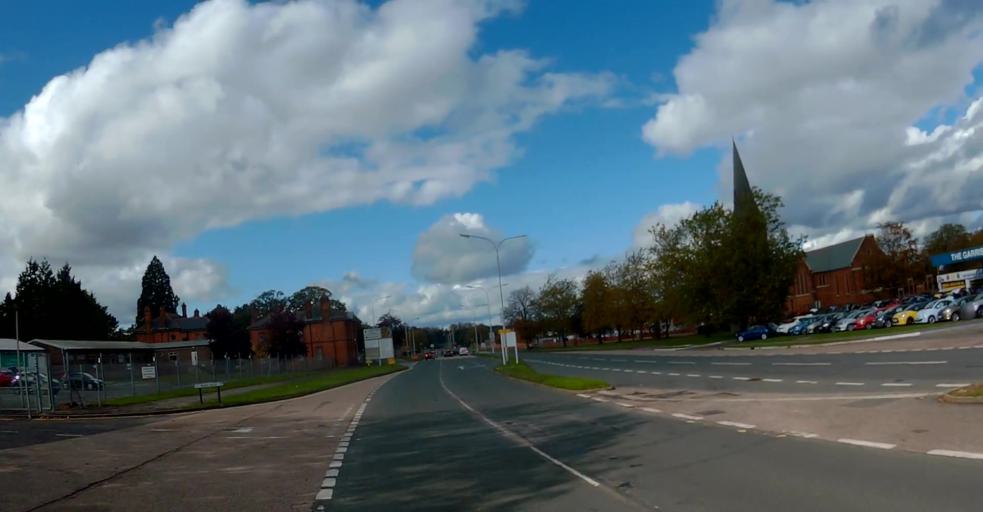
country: GB
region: England
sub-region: Hampshire
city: Aldershot
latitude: 51.2588
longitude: -0.7590
